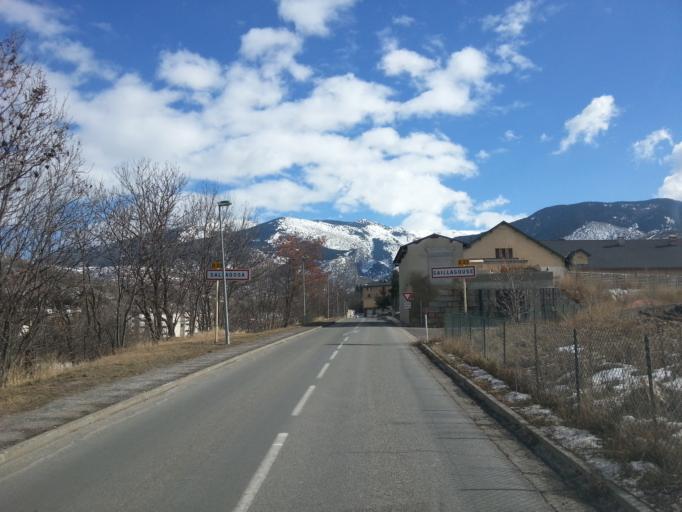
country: ES
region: Catalonia
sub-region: Provincia de Girona
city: Llivia
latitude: 42.4570
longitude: 2.0336
